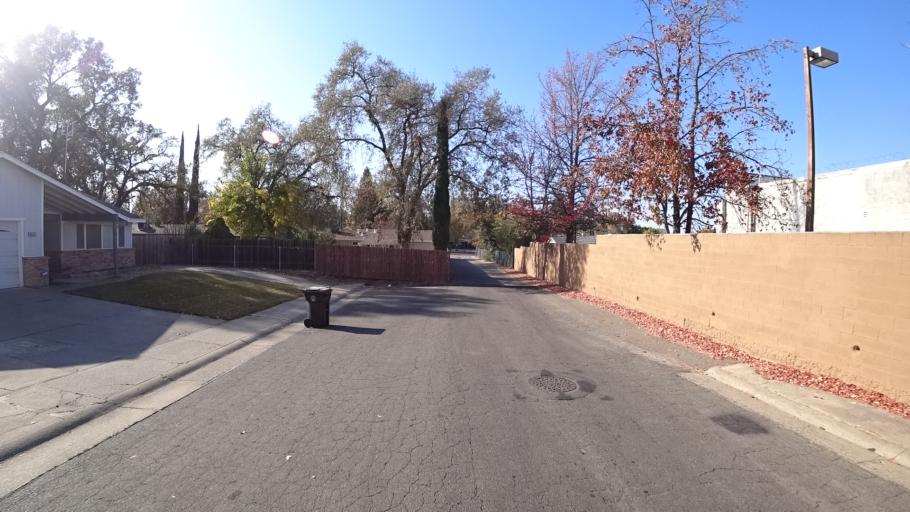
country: US
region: California
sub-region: Sacramento County
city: Citrus Heights
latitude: 38.6772
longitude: -121.2838
